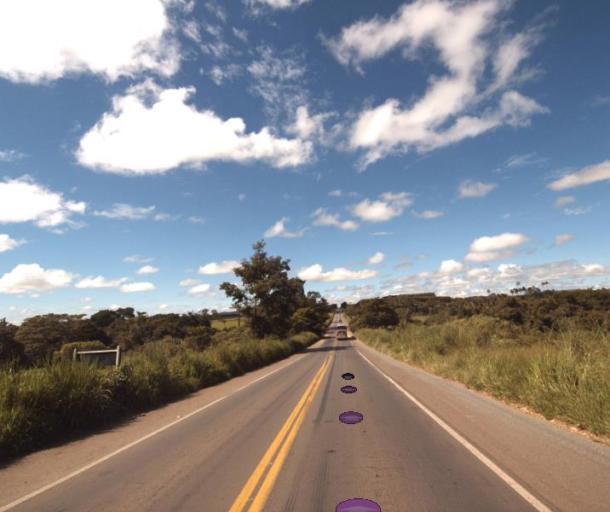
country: BR
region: Goias
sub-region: Rialma
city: Rialma
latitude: -15.4556
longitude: -49.5029
